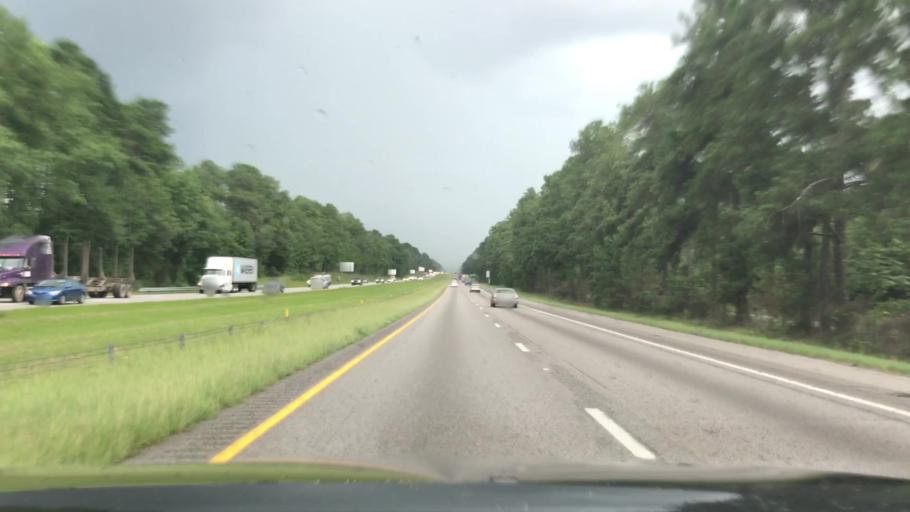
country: US
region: South Carolina
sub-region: Orangeburg County
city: Brookdale
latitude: 33.5529
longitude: -80.8190
